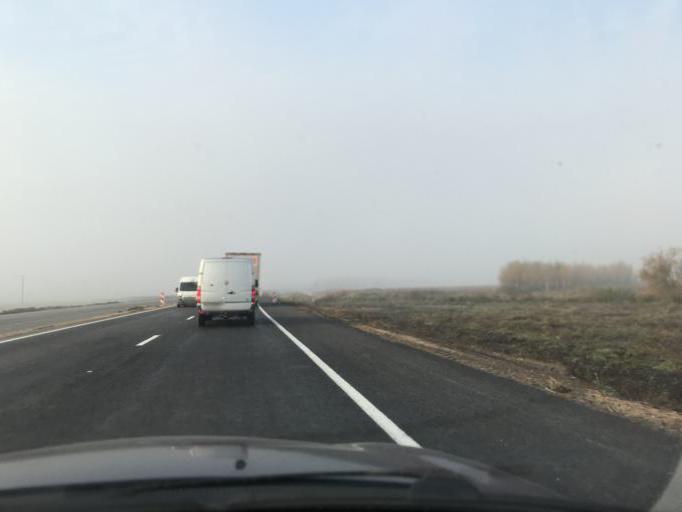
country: BY
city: Berezovka
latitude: 53.8358
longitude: 25.4665
